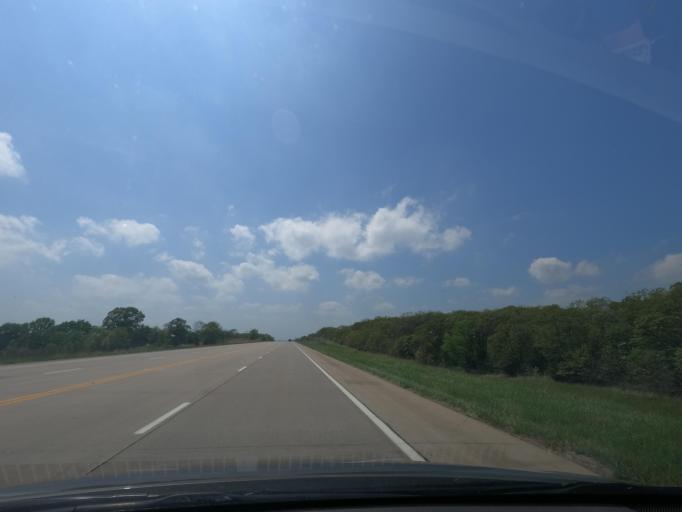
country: US
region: Kansas
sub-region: Wilson County
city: Fredonia
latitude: 37.6143
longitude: -95.9114
